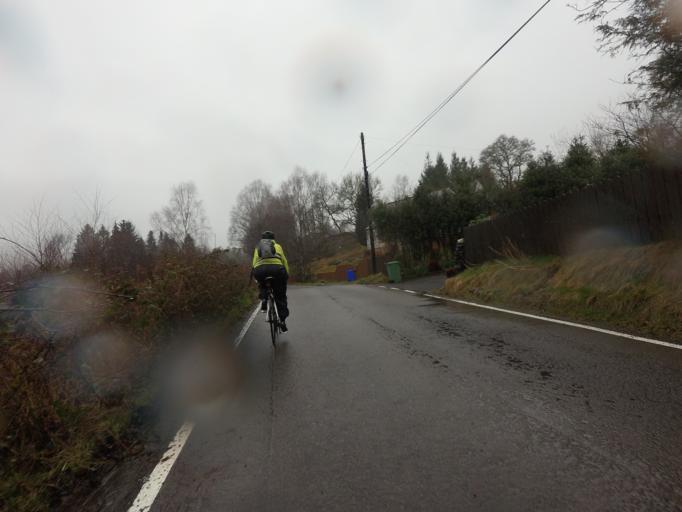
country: GB
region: Scotland
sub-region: Stirling
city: Killearn
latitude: 56.1890
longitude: -4.4945
